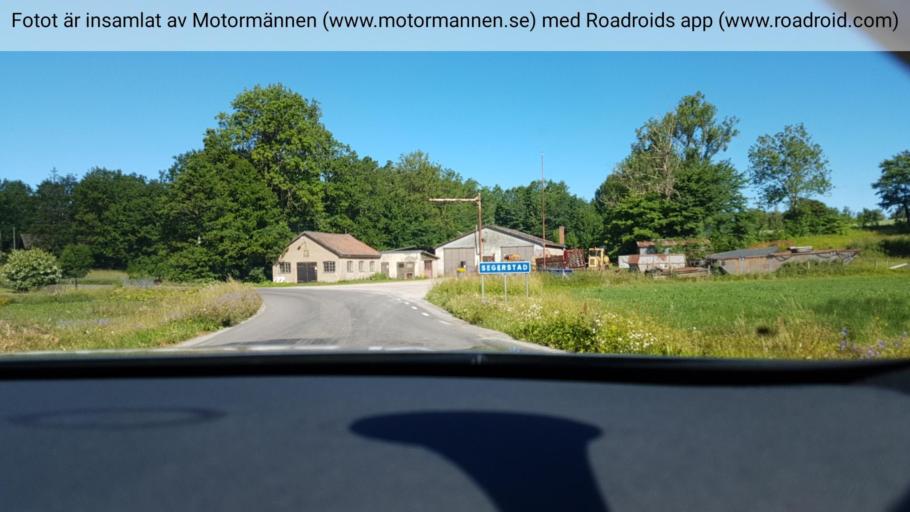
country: SE
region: Vaestra Goetaland
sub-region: Falkopings Kommun
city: Akarp
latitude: 58.2572
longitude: 13.6703
